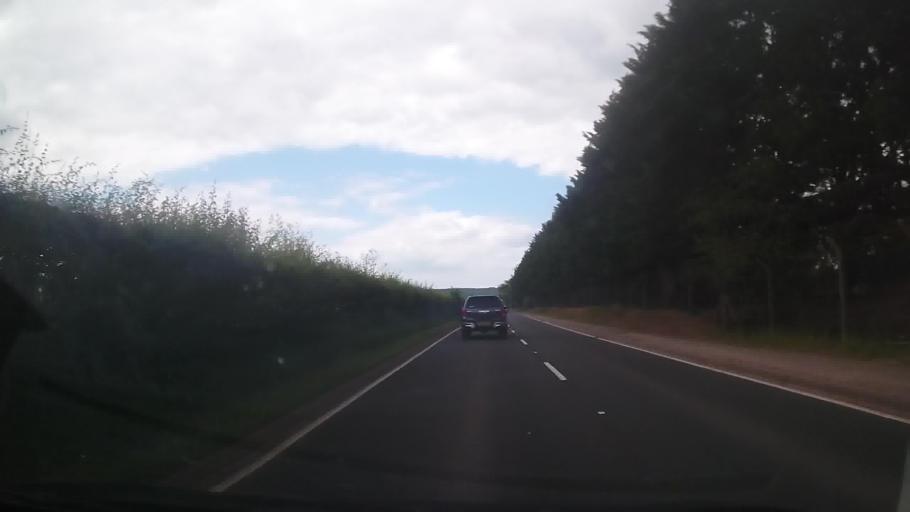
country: GB
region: England
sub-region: Herefordshire
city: Wellington
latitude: 52.1248
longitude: -2.7318
